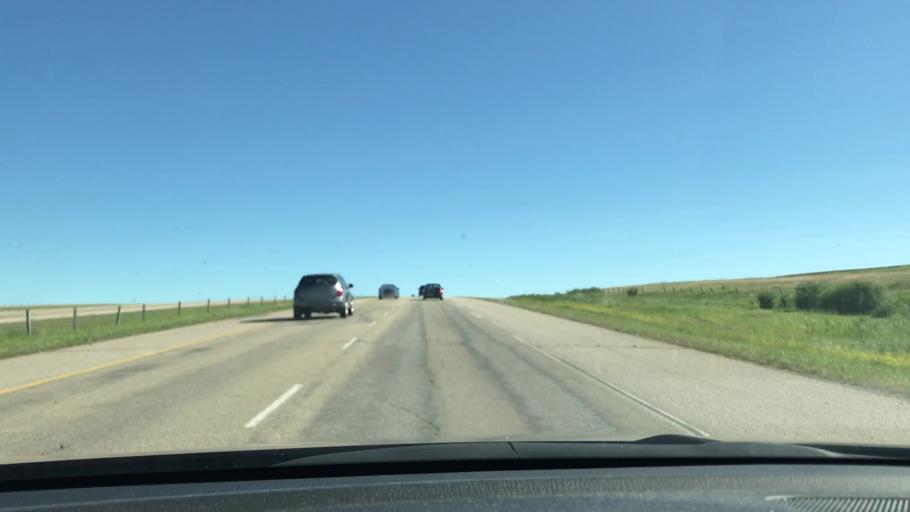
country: CA
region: Alberta
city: Carstairs
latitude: 51.5961
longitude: -114.0254
